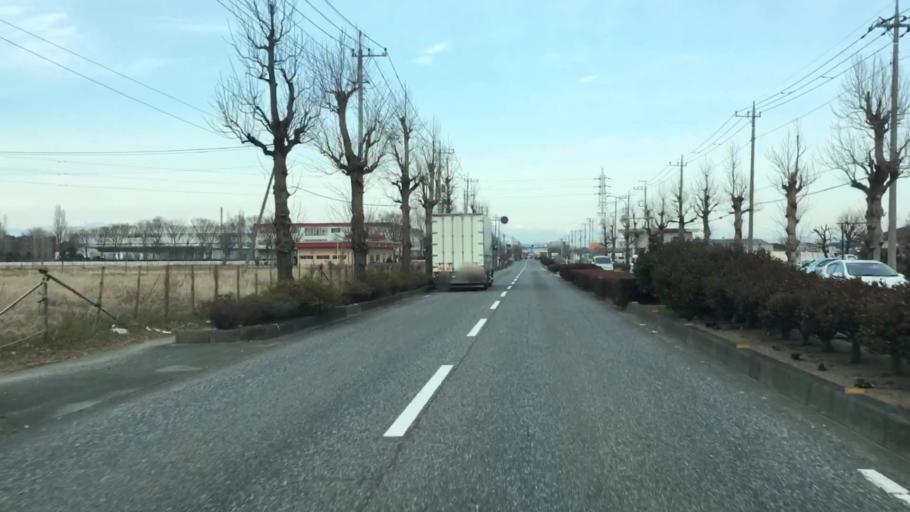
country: JP
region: Saitama
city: Menuma
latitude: 36.1971
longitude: 139.3704
